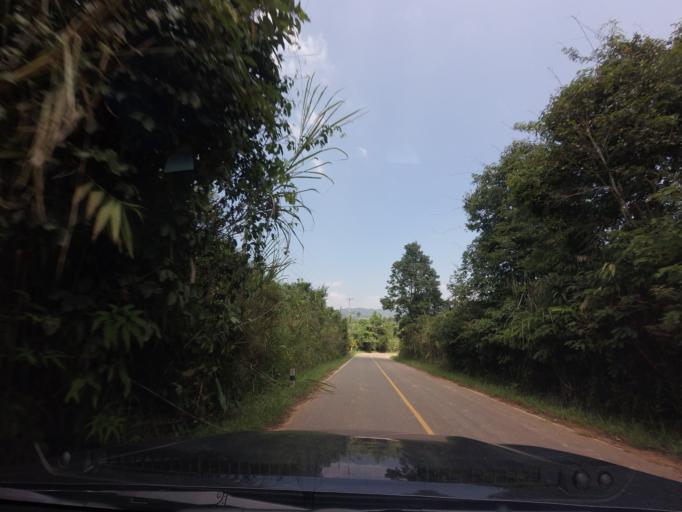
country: TH
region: Loei
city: Na Haeo
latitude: 17.5299
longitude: 100.8794
